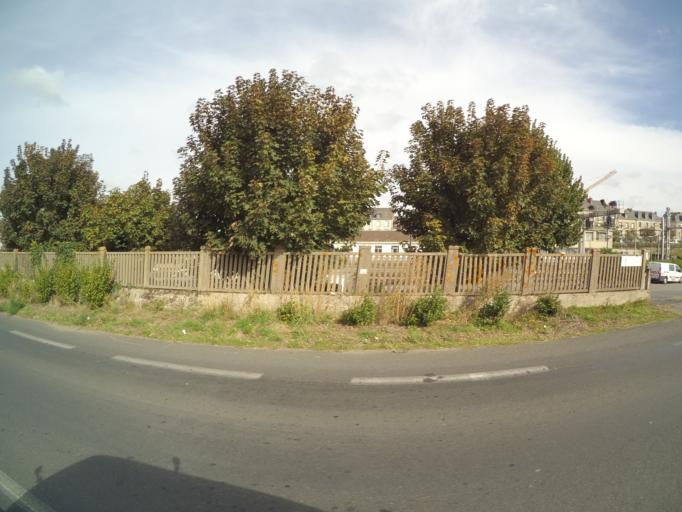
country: FR
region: Pays de la Loire
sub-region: Departement de Maine-et-Loire
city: Saumur
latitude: 47.2680
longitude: -0.0714
